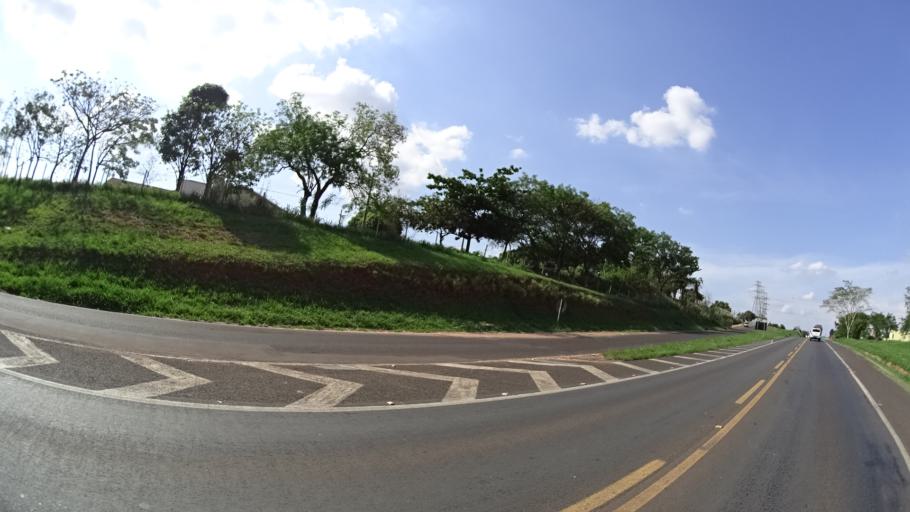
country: BR
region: Sao Paulo
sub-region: Sao Jose Do Rio Preto
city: Sao Jose do Rio Preto
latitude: -20.8457
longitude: -49.3736
